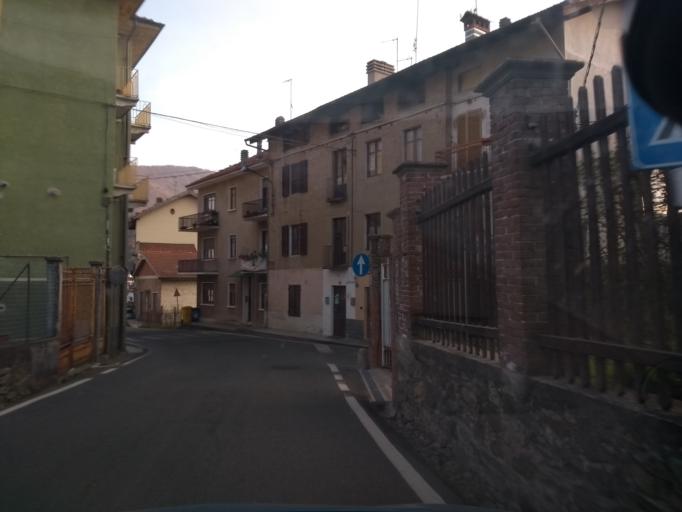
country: IT
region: Piedmont
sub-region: Provincia di Torino
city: Lanzo Torinese
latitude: 45.2773
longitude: 7.4809
